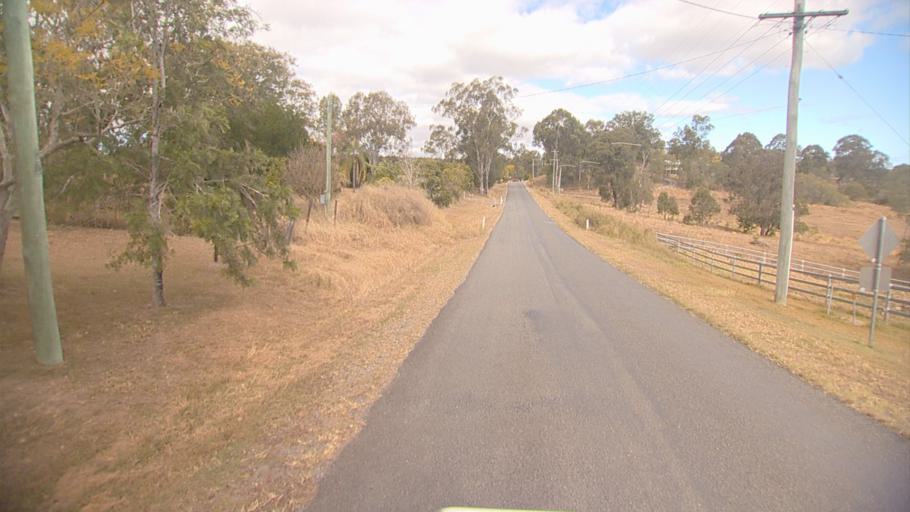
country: AU
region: Queensland
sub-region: Logan
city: Cedar Vale
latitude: -27.8799
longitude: 153.0278
